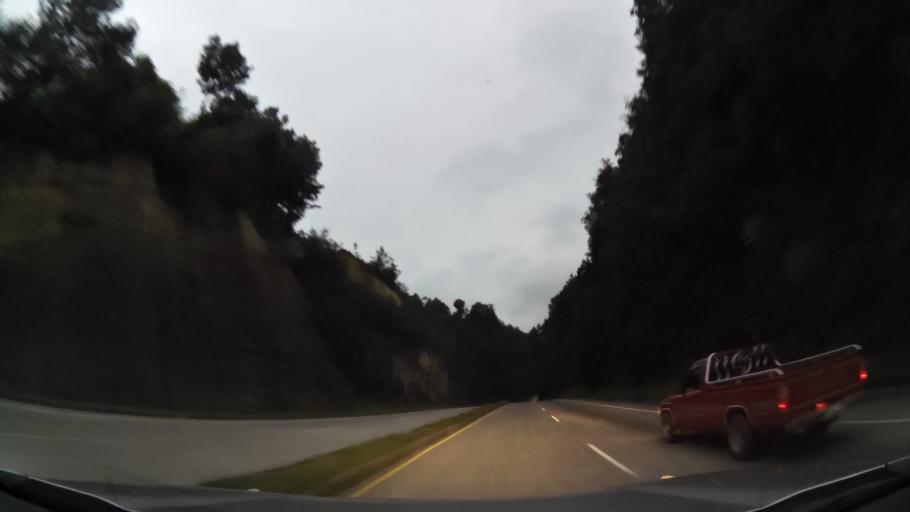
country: GT
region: Chimaltenango
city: Tecpan Guatemala
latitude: 14.8296
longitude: -91.0390
